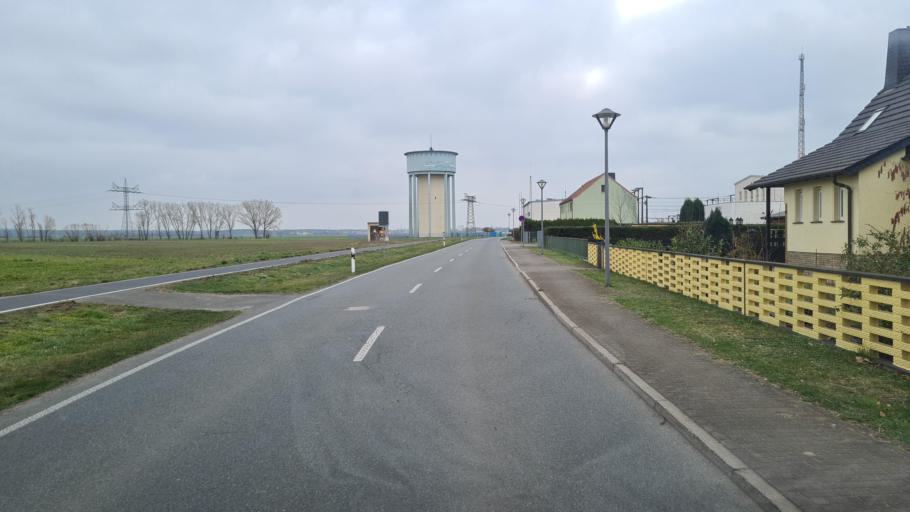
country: DE
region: Saxony
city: Nauwalde
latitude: 51.4064
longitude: 13.4519
